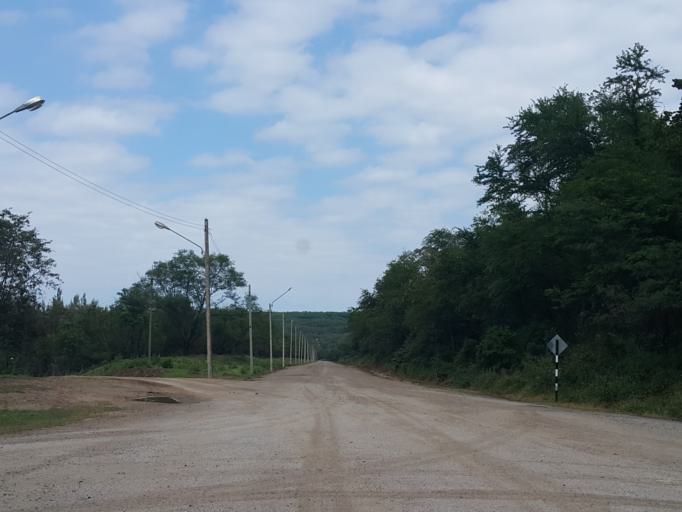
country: TH
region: Lampang
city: Mae Mo
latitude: 18.3158
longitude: 99.7470
